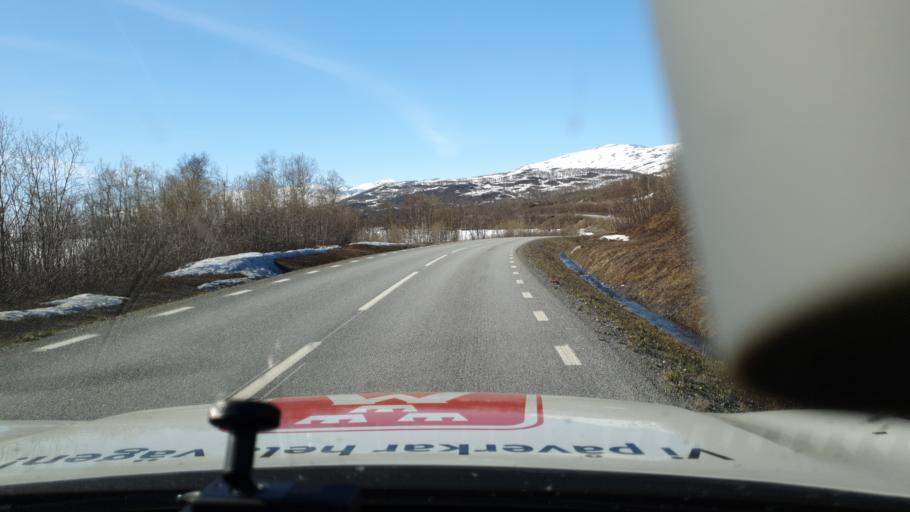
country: NO
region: Nordland
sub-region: Rana
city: Mo i Rana
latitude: 66.0857
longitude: 14.8597
